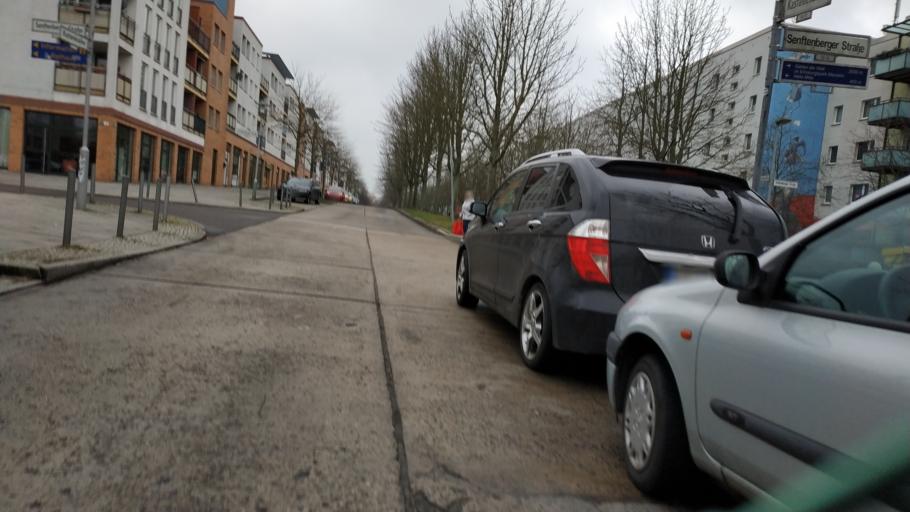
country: DE
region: Berlin
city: Hellersdorf
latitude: 52.5386
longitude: 13.6007
